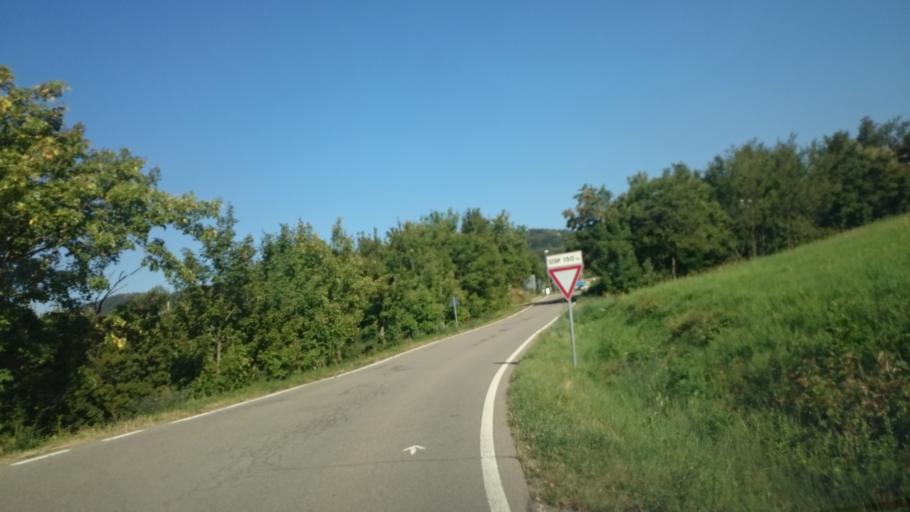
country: IT
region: Emilia-Romagna
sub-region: Provincia di Reggio Emilia
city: Villa Minozzo
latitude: 44.2975
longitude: 10.4536
